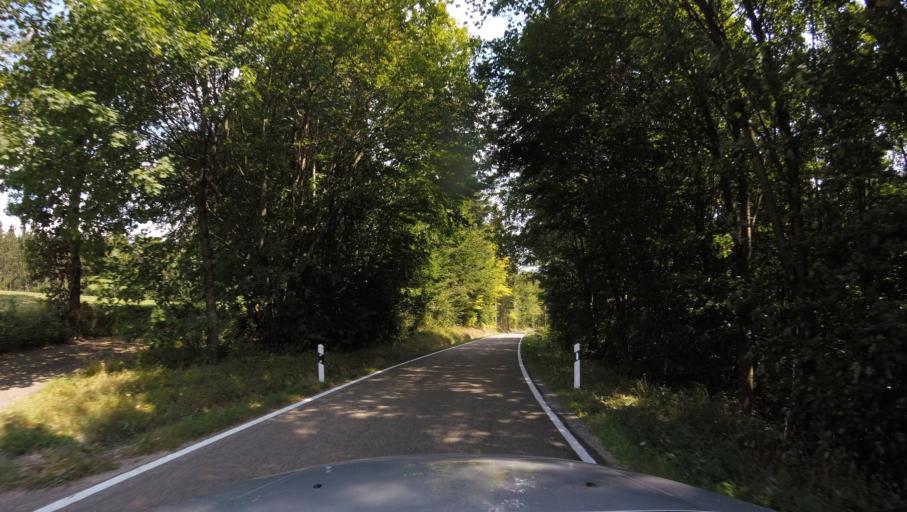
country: DE
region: Baden-Wuerttemberg
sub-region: Regierungsbezirk Stuttgart
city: Alfdorf
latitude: 48.8784
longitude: 9.6872
